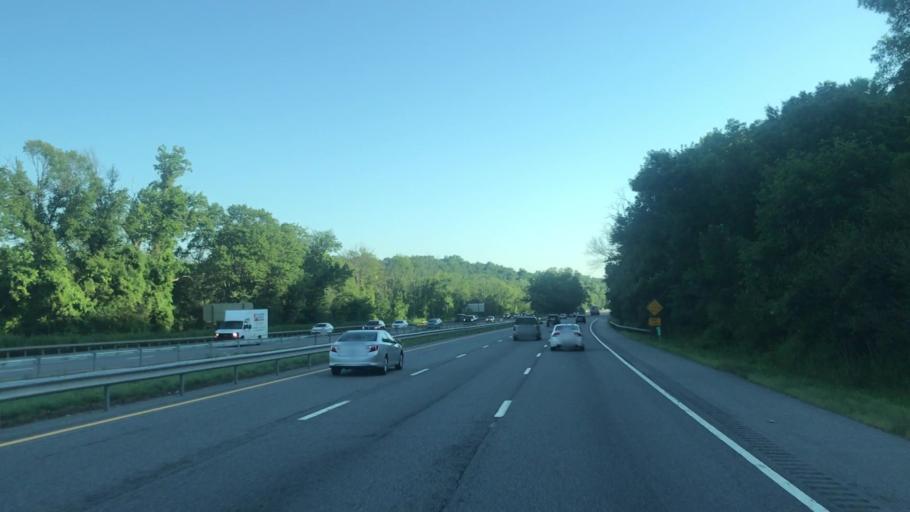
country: US
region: New York
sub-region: Westchester County
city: Armonk
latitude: 41.0923
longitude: -73.7175
